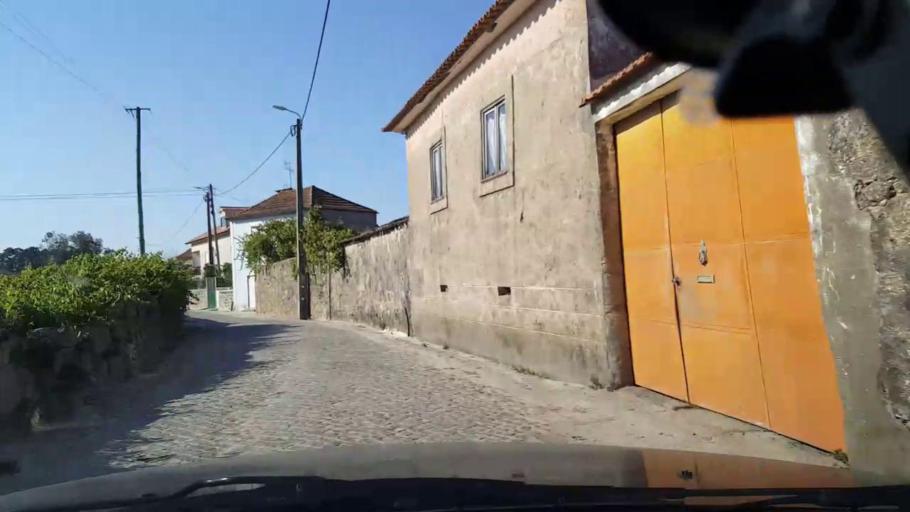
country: PT
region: Porto
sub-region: Vila do Conde
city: Arvore
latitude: 41.3593
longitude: -8.7201
